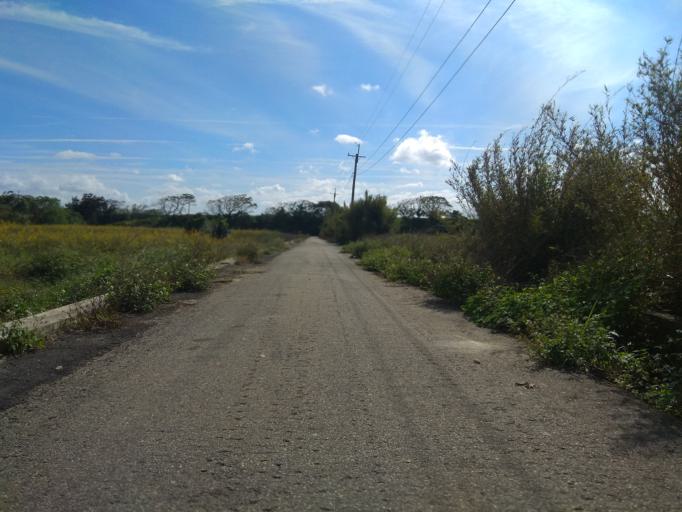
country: TW
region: Taiwan
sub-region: Hsinchu
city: Zhubei
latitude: 25.0166
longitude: 121.0662
